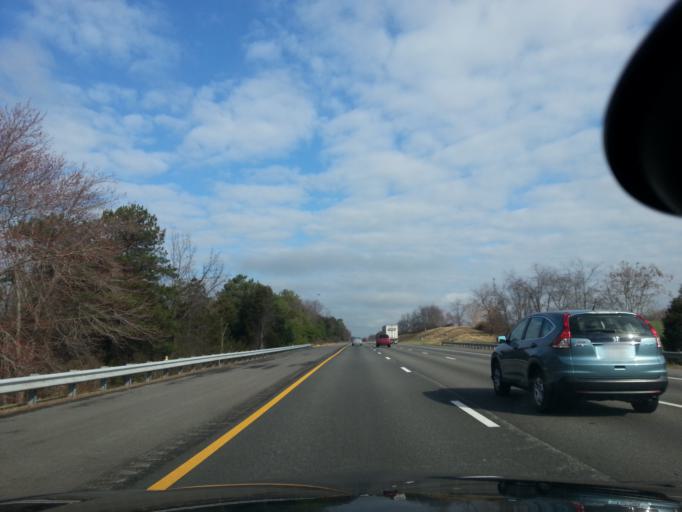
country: US
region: Virginia
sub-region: Spotsylvania County
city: Spotsylvania Courthouse
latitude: 38.0716
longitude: -77.5097
